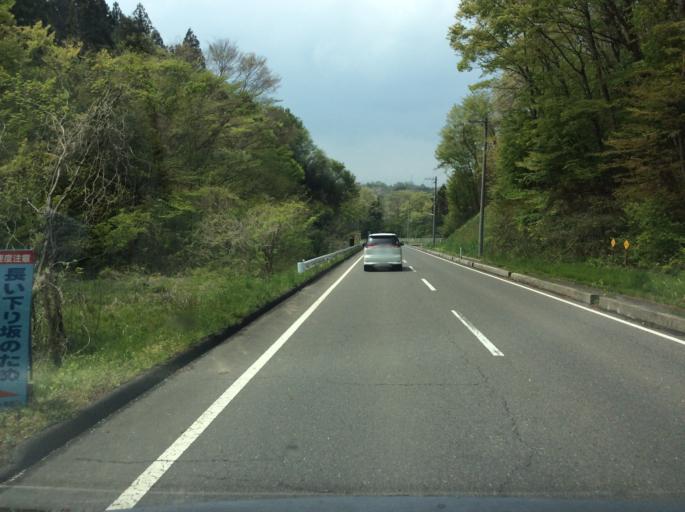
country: JP
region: Fukushima
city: Miharu
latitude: 37.4006
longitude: 140.4742
